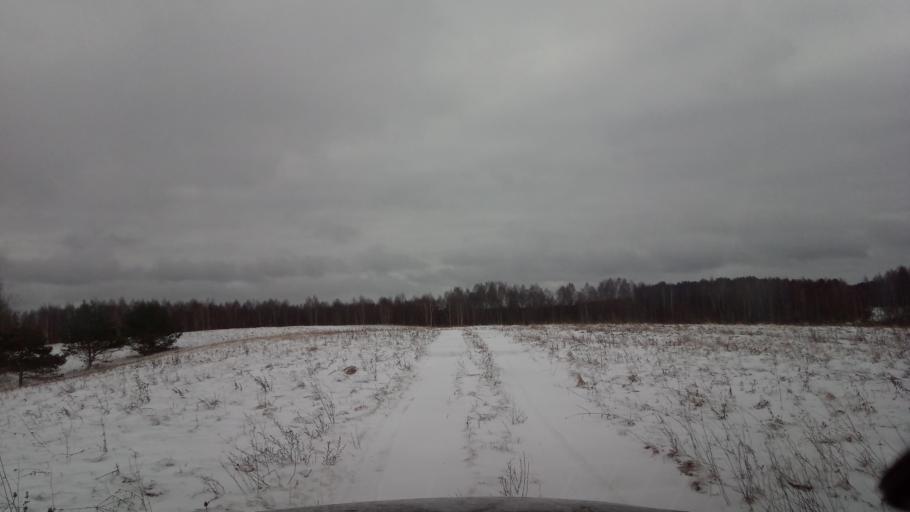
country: LT
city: Zarasai
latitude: 55.6890
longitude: 26.0912
